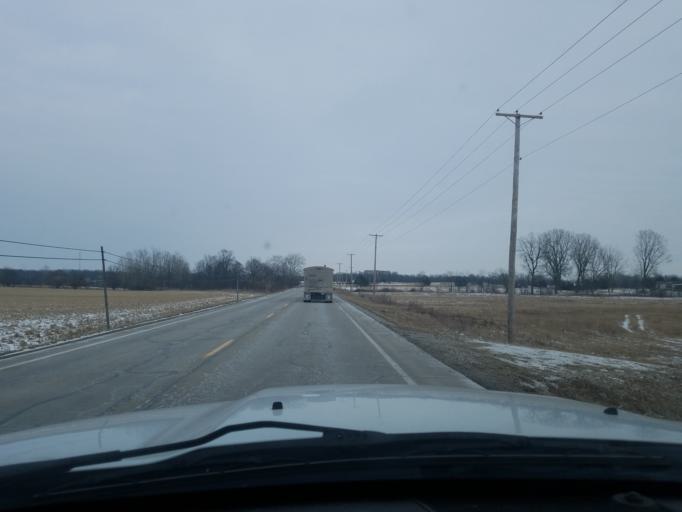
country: US
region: Indiana
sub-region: Randolph County
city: Lynn
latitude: 40.0487
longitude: -84.9671
